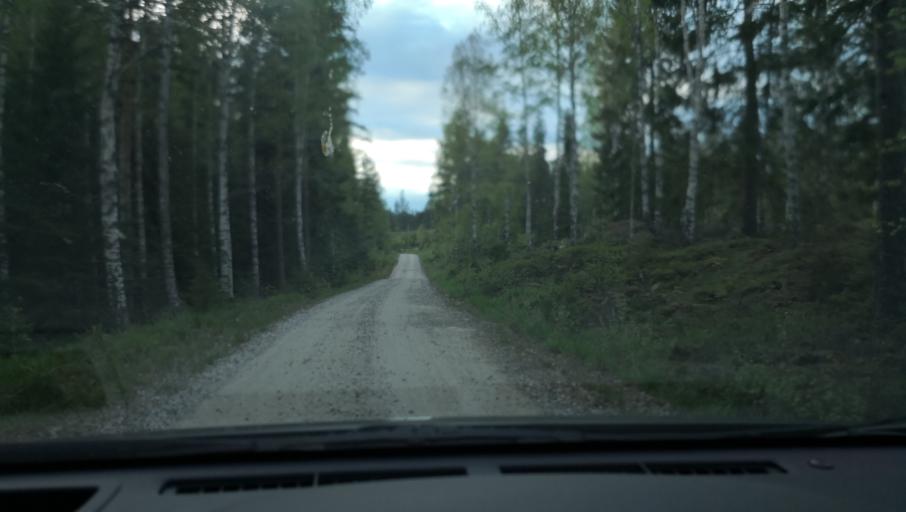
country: SE
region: Vaestmanland
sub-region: Skinnskattebergs Kommun
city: Skinnskatteberg
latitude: 59.7966
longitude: 15.4634
